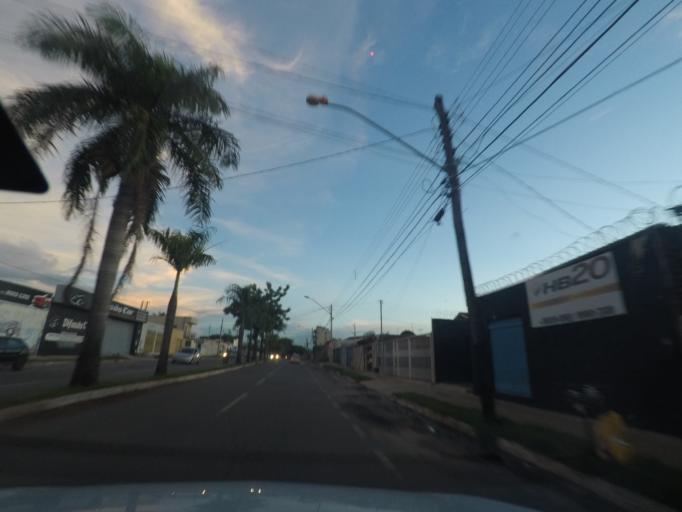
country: BR
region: Goias
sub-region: Goiania
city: Goiania
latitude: -16.7024
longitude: -49.3114
